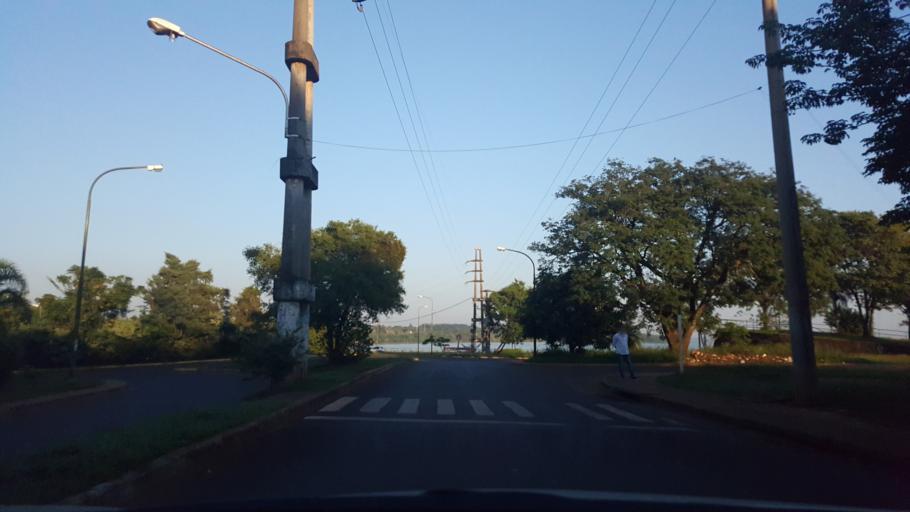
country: AR
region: Misiones
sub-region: Departamento de Capital
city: Posadas
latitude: -27.3717
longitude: -55.9527
